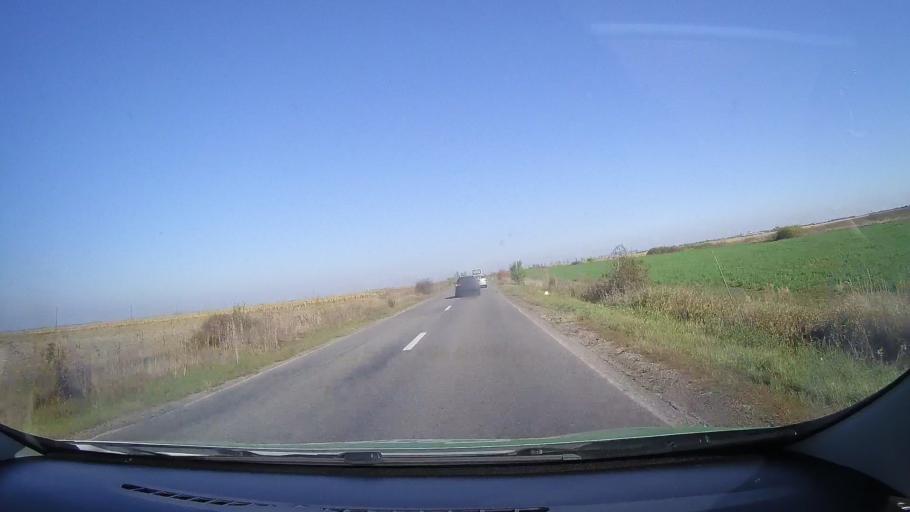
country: RO
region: Satu Mare
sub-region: Comuna Cauas
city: Cauas
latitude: 47.5813
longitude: 22.5478
